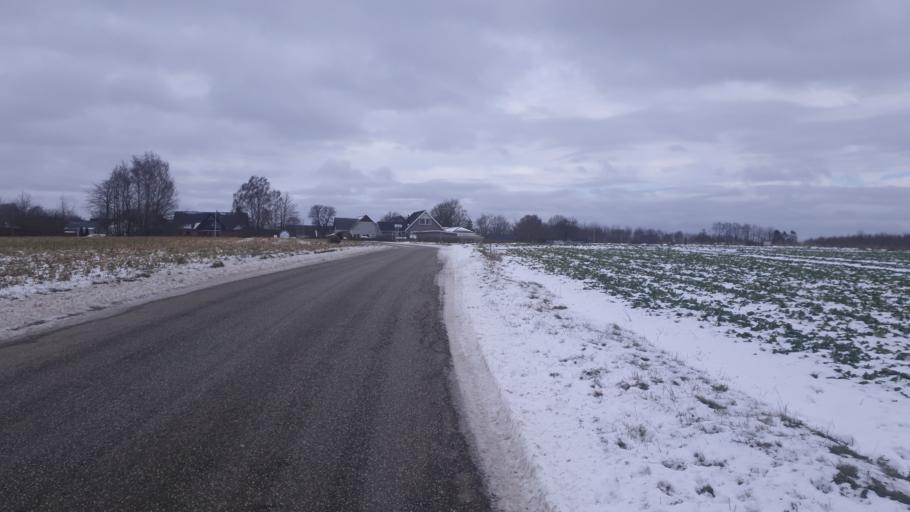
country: DK
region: Central Jutland
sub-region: Hedensted Kommune
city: Hedensted
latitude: 55.8003
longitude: 9.7057
